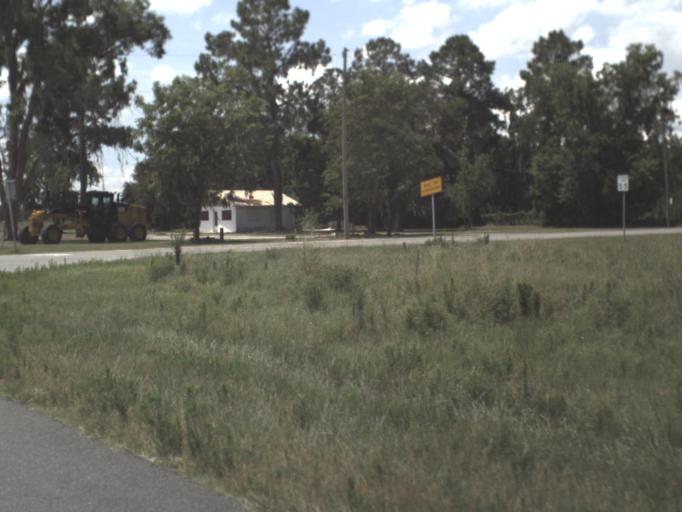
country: US
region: Florida
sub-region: Hamilton County
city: Jasper
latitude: 30.4005
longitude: -82.8354
